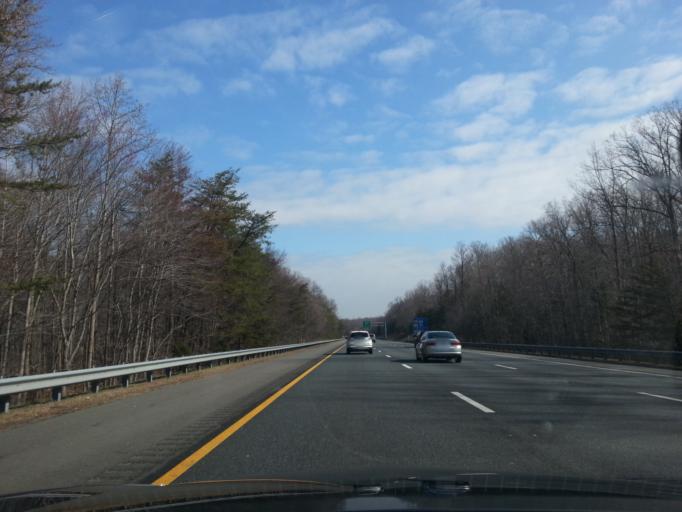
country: US
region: Virginia
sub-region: Stafford County
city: Stafford
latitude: 38.4380
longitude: -77.4119
